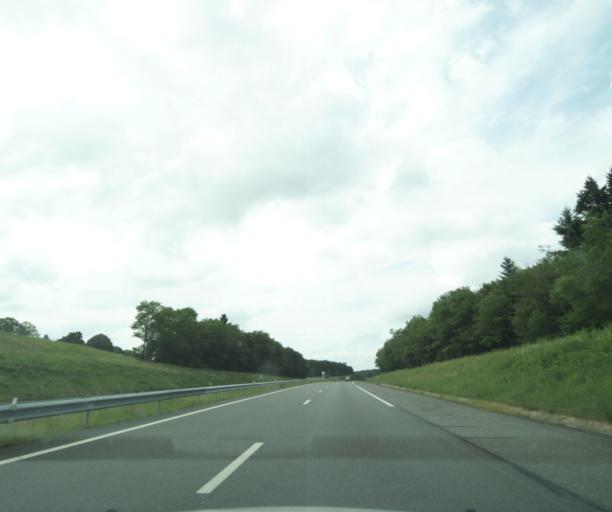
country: FR
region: Centre
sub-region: Departement du Cher
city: Orval
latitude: 46.7534
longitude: 2.4157
